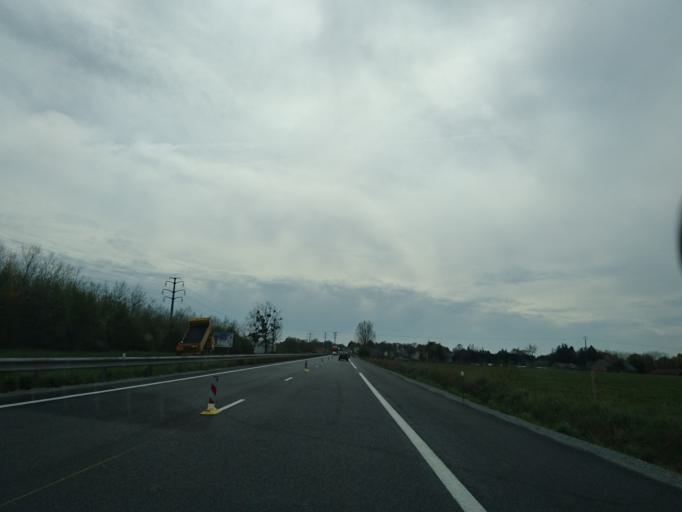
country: FR
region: Brittany
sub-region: Departement des Cotes-d'Armor
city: Quevert
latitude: 48.4644
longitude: -2.0668
